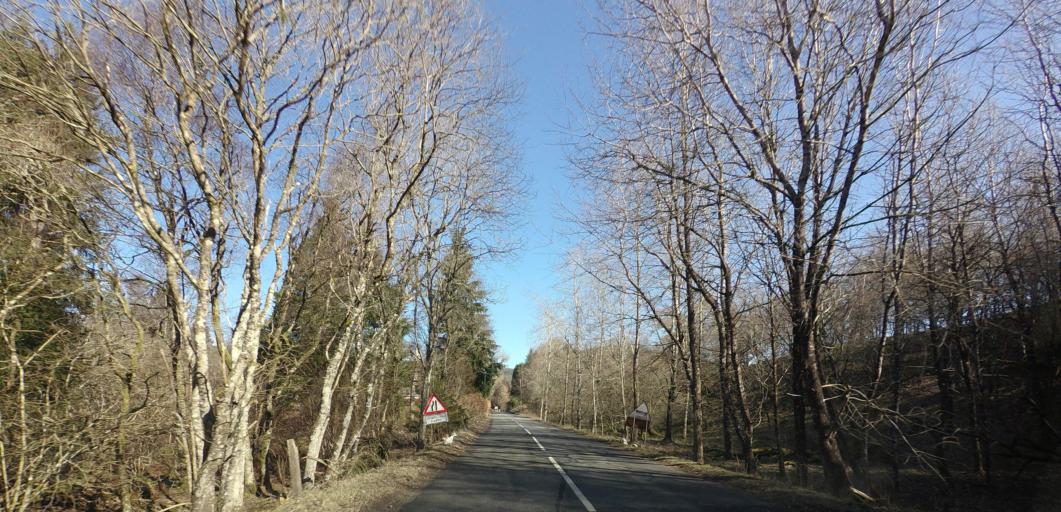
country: GB
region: Scotland
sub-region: Perth and Kinross
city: Methven
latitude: 56.5386
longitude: -3.6647
